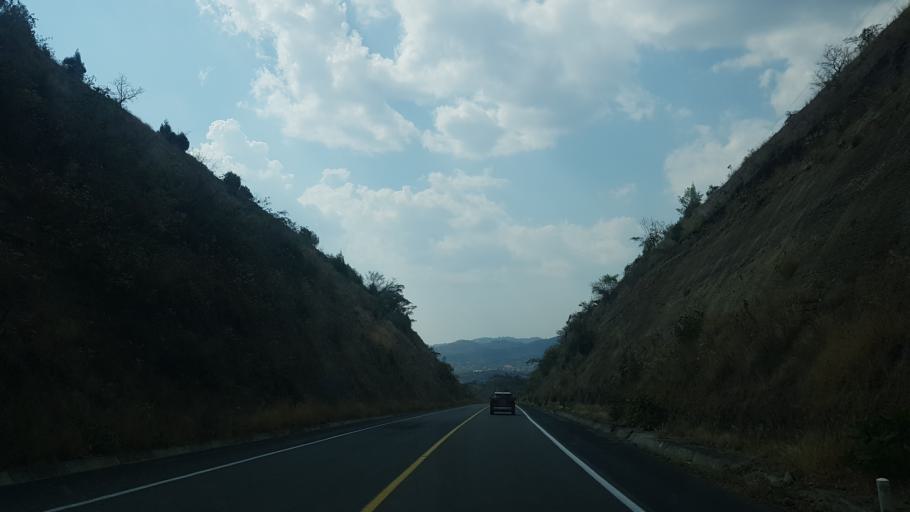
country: MX
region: Puebla
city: San Juan Amecac
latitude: 18.8179
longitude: -98.6807
